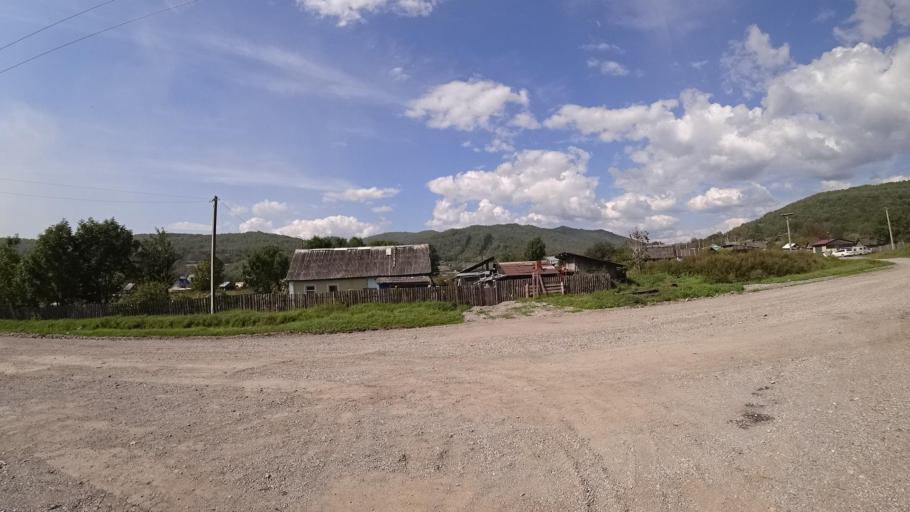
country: RU
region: Jewish Autonomous Oblast
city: Londoko
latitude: 49.0260
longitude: 131.9322
